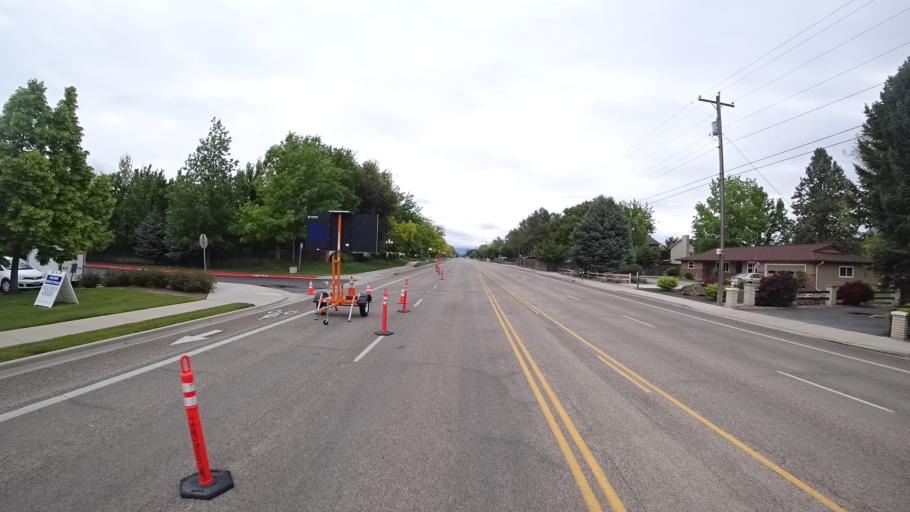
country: US
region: Idaho
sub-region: Ada County
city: Eagle
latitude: 43.6485
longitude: -116.3325
